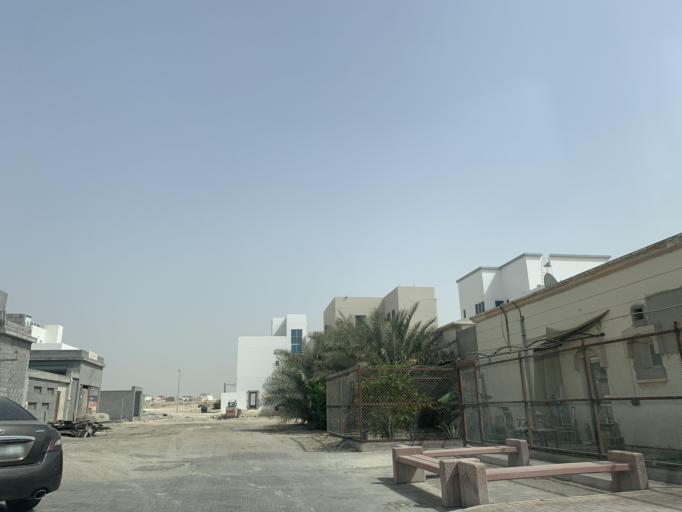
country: BH
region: Central Governorate
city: Madinat Hamad
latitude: 26.1531
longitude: 50.5093
